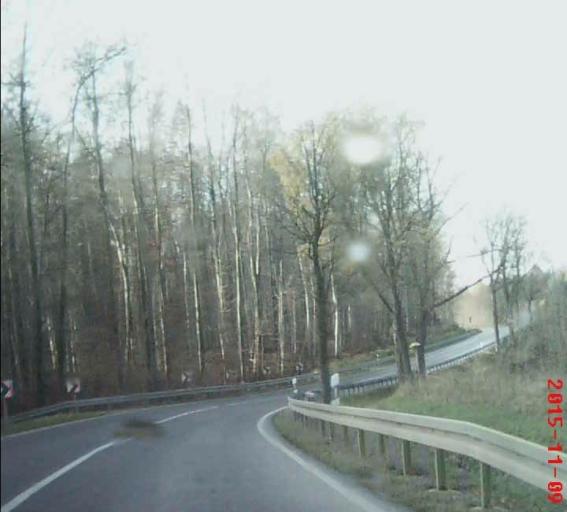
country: DE
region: Thuringia
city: Heyerode
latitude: 51.1997
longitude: 10.3132
